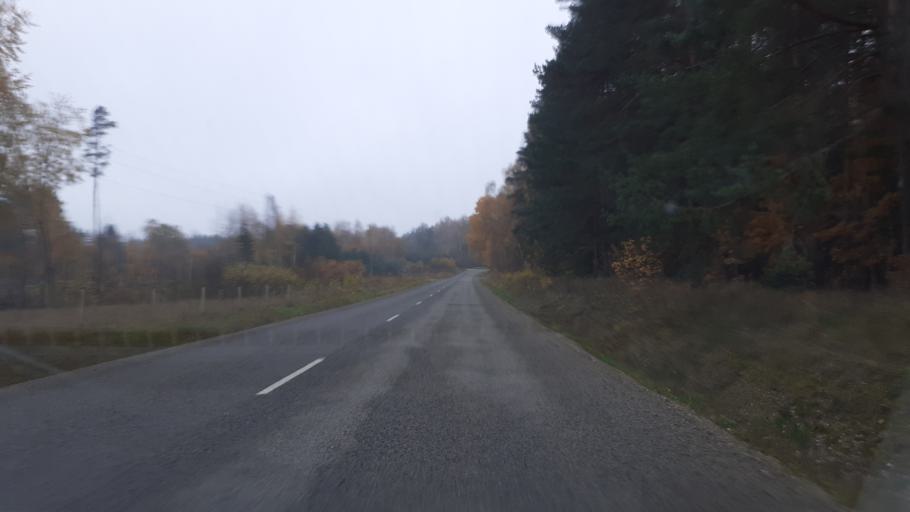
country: LV
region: Kuldigas Rajons
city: Kuldiga
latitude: 56.9573
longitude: 21.8867
